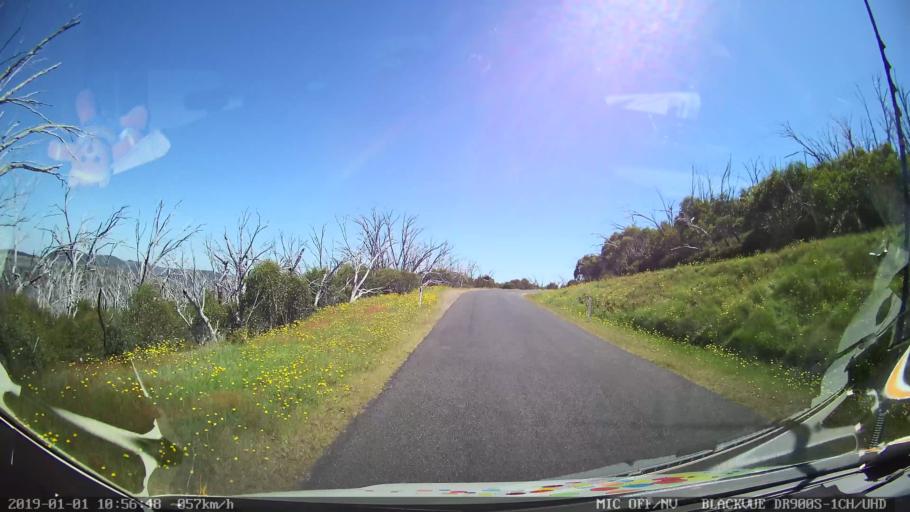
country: AU
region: New South Wales
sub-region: Snowy River
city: Jindabyne
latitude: -36.0018
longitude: 148.3941
